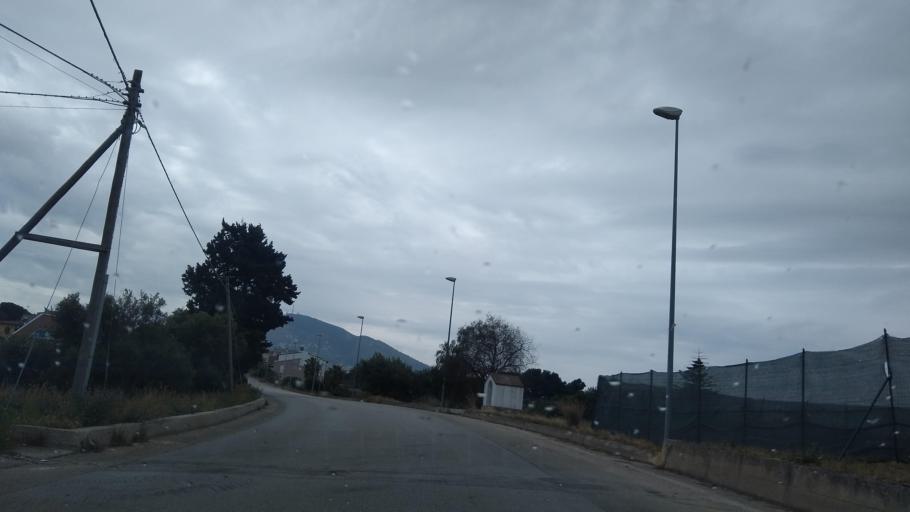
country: IT
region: Sicily
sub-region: Trapani
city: Alcamo
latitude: 38.0079
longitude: 12.9541
